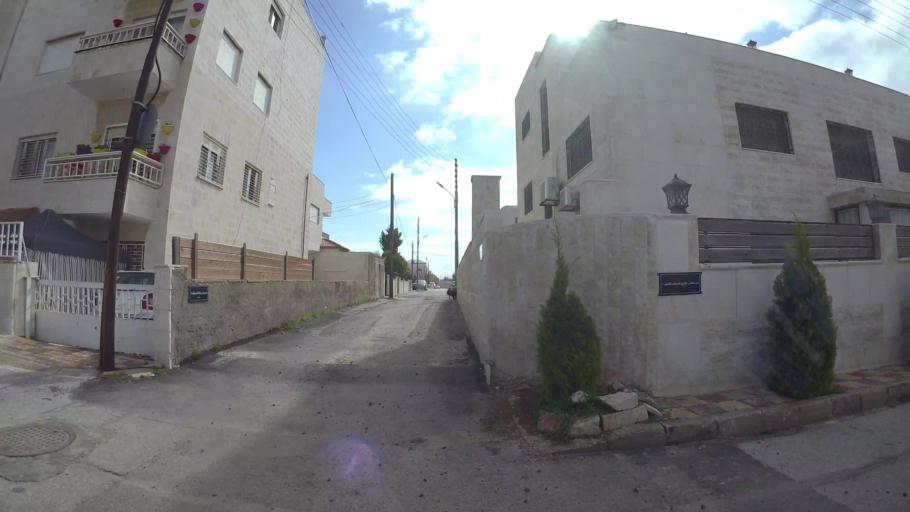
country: JO
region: Amman
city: Wadi as Sir
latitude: 31.9491
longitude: 35.8460
